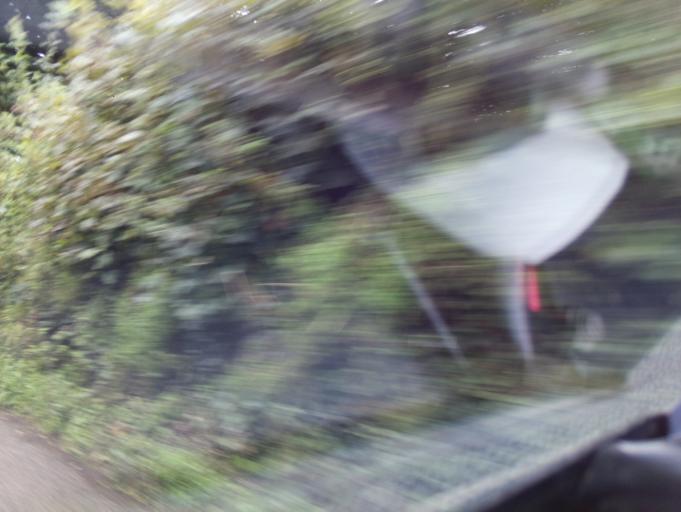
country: GB
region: England
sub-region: Devon
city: Totnes
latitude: 50.3529
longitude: -3.6625
